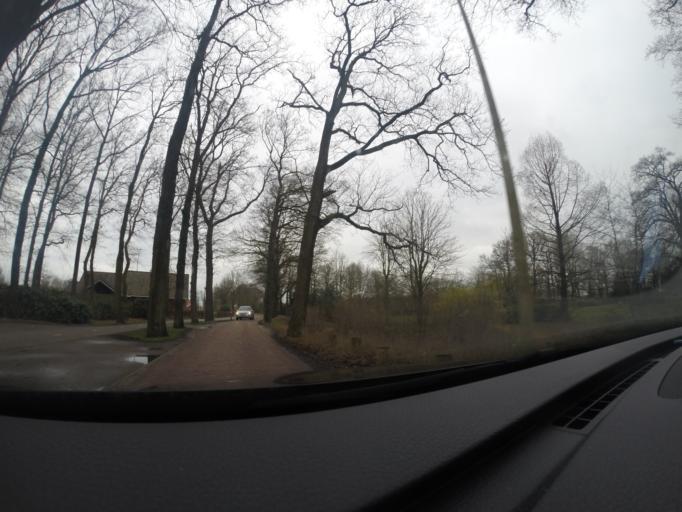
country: NL
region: Overijssel
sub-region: Gemeente Haaksbergen
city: Haaksbergen
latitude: 52.1456
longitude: 6.7274
